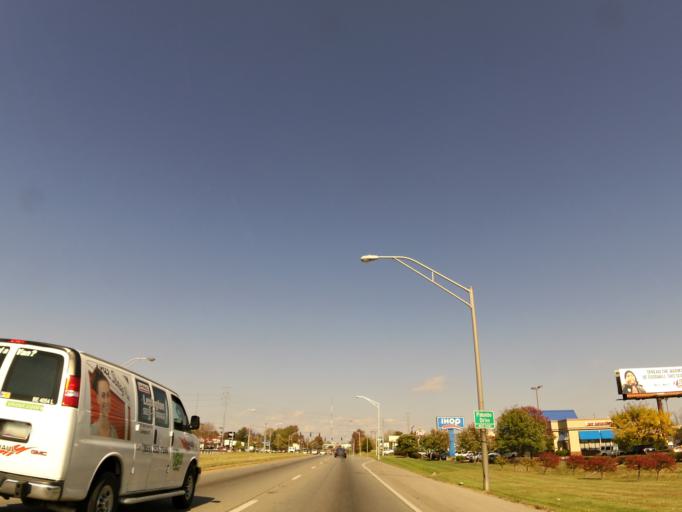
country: US
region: Kentucky
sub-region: Fayette County
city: Lexington-Fayette
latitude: 38.0211
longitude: -84.4552
